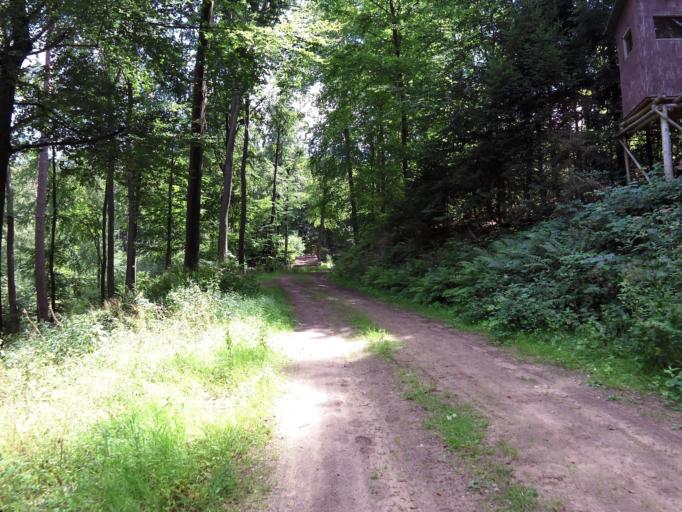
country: DE
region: Rheinland-Pfalz
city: Altleiningen
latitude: 49.4644
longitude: 8.0670
